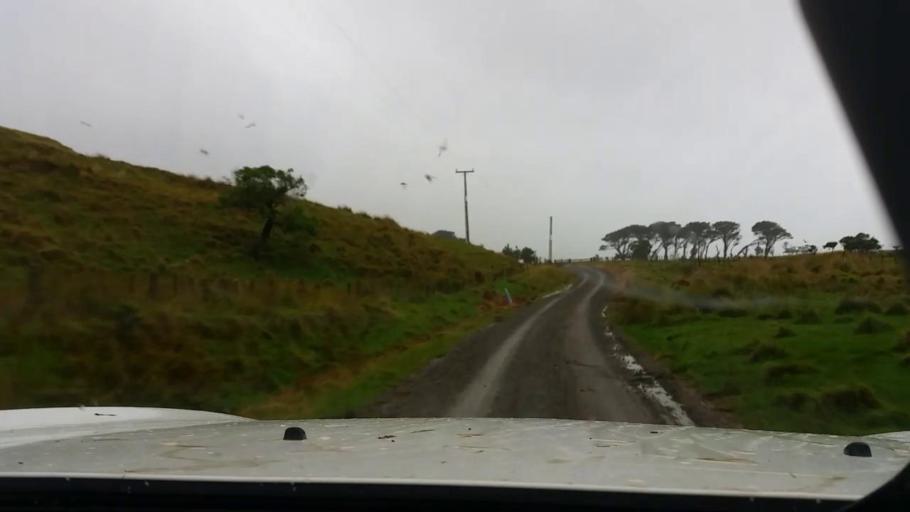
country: NZ
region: Wellington
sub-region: Masterton District
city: Masterton
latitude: -41.2640
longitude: 175.8922
